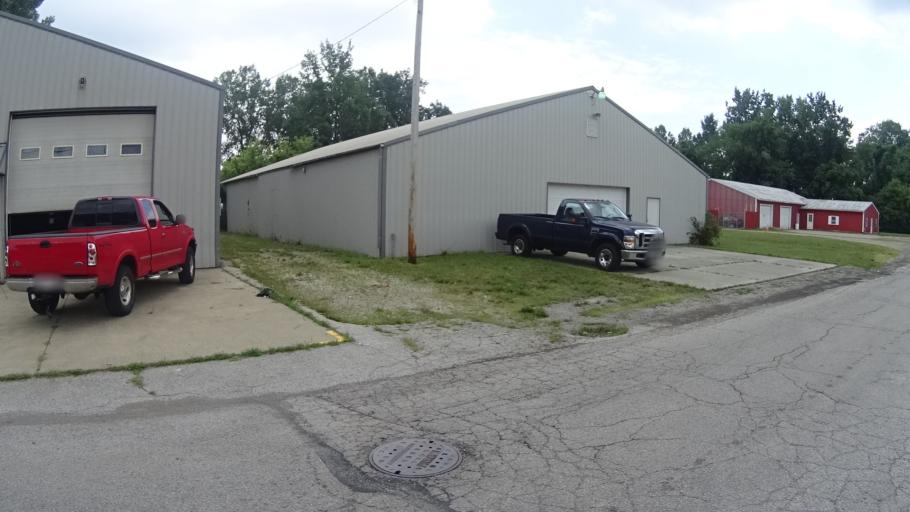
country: US
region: Ohio
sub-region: Erie County
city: Sandusky
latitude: 41.4397
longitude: -82.7512
